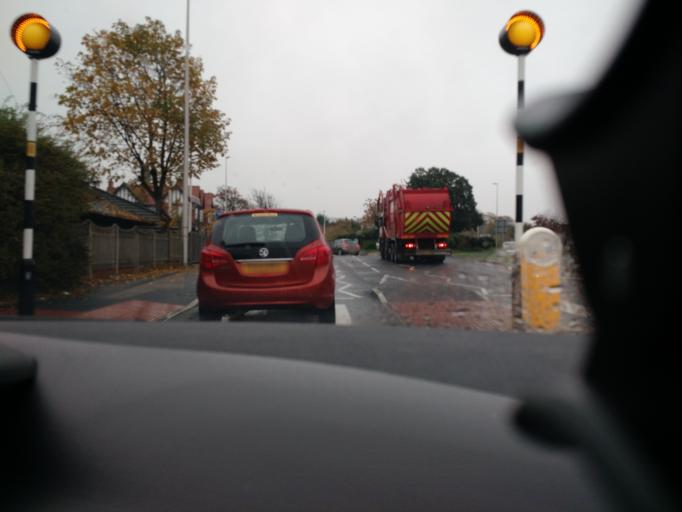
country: GB
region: England
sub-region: Lancashire
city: Great Marton
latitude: 53.8238
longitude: -3.0182
